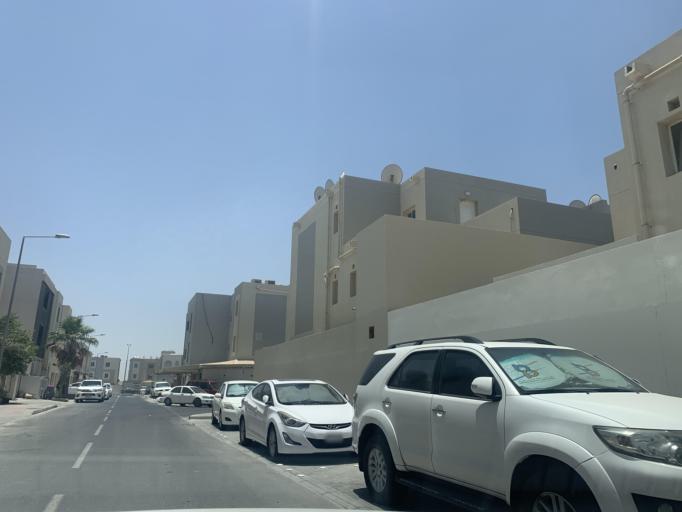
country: BH
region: Manama
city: Jidd Hafs
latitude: 26.2361
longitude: 50.4581
